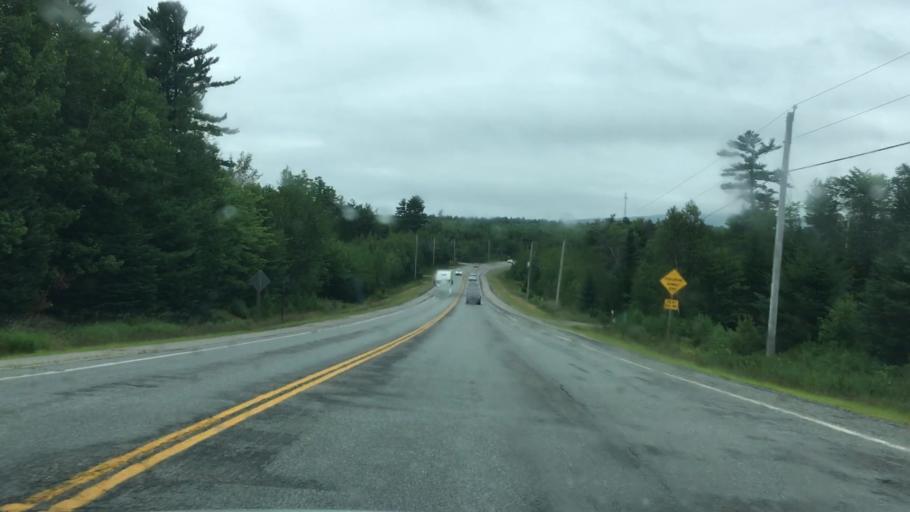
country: US
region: Maine
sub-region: Washington County
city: Cherryfield
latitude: 44.8498
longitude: -68.0607
